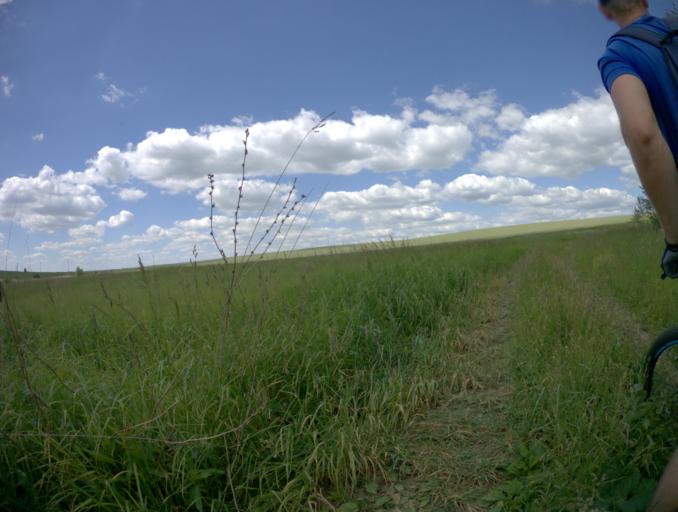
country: RU
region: Vladimir
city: Vladimir
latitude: 56.2541
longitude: 40.4104
